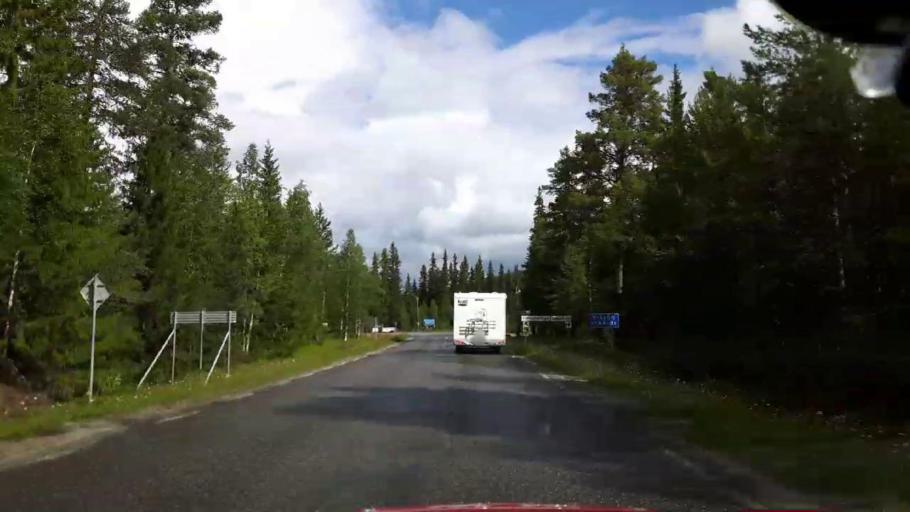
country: SE
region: Vaesterbotten
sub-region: Vilhelmina Kommun
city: Sjoberg
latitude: 64.9371
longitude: 15.8583
